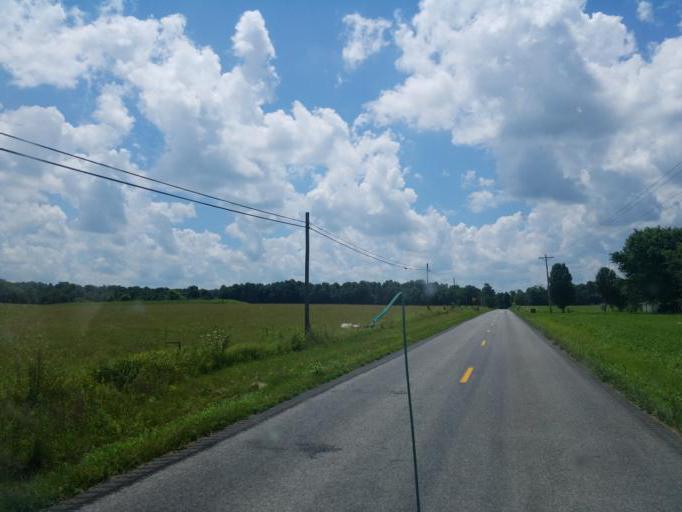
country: US
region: Kentucky
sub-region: Grayson County
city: Leitchfield
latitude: 37.5142
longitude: -86.4723
